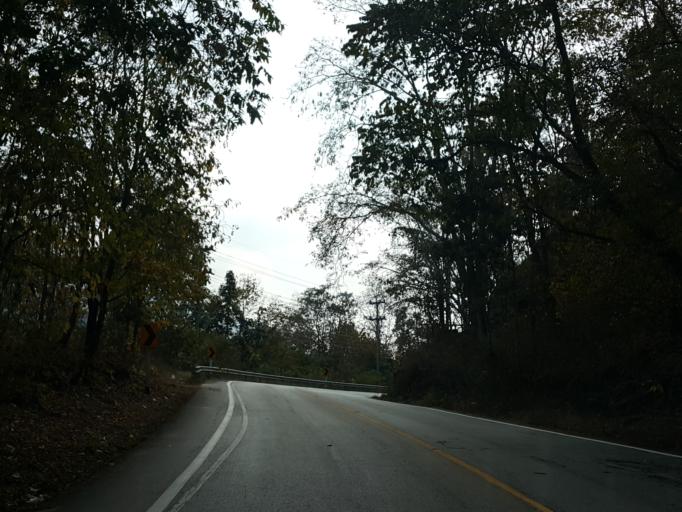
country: TH
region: Chiang Mai
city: Hot
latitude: 18.2009
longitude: 98.4505
